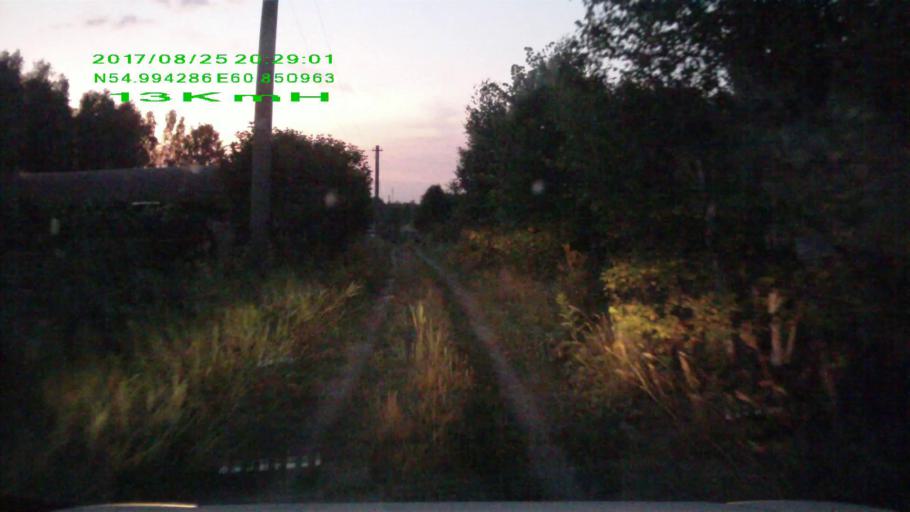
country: RU
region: Chelyabinsk
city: Timiryazevskiy
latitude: 54.9944
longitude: 60.8509
